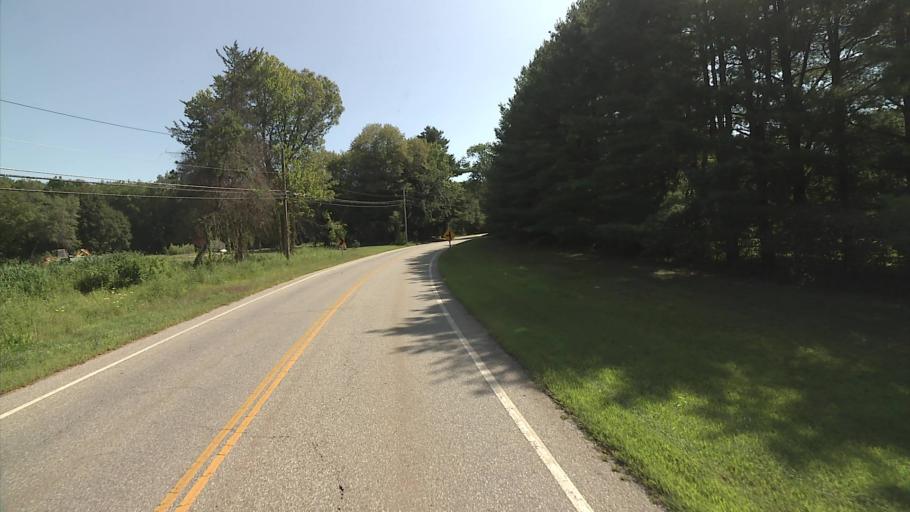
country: US
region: Connecticut
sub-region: New London County
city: Colchester
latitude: 41.6199
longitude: -72.2663
